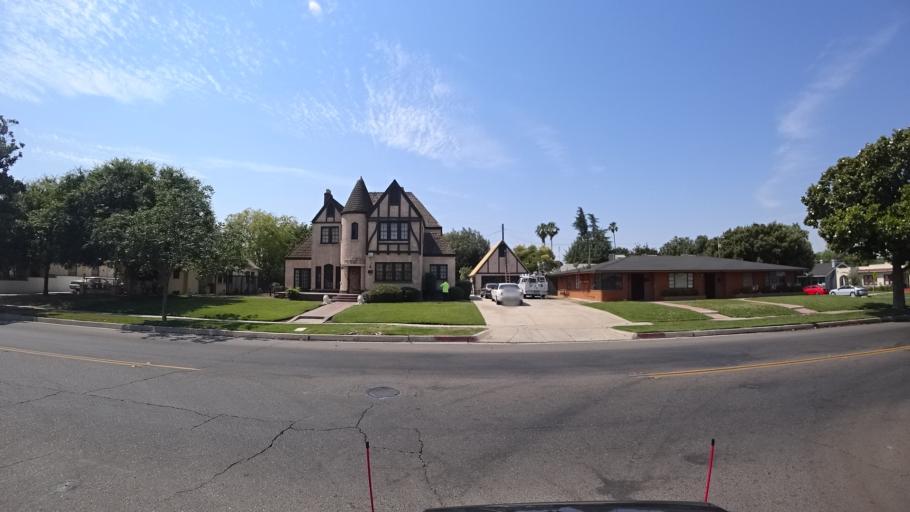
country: US
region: California
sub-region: Fresno County
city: Fresno
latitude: 36.7578
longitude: -119.7923
